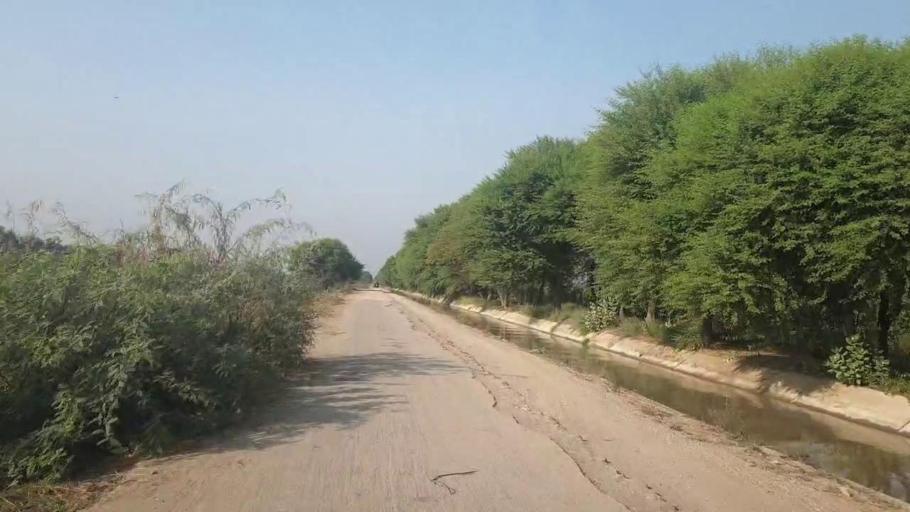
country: PK
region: Sindh
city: Tando Jam
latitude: 25.4223
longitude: 68.4620
